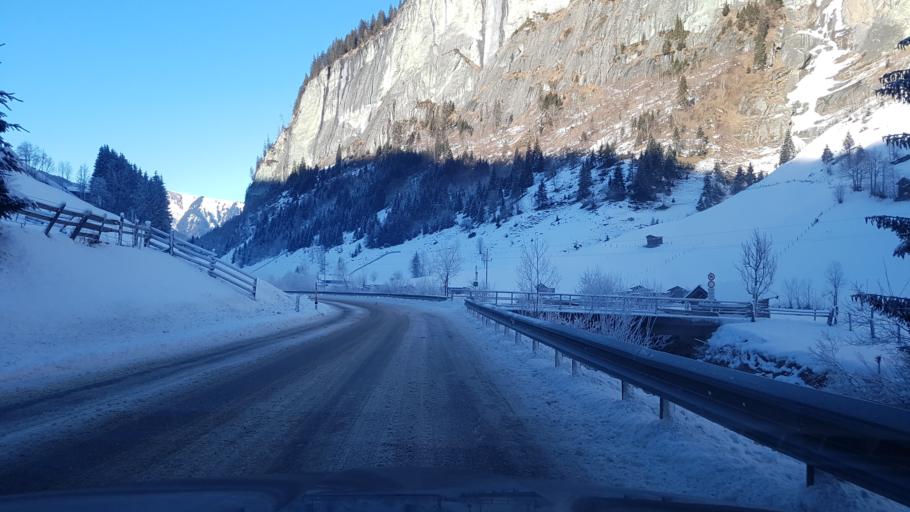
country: AT
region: Salzburg
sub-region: Politischer Bezirk Sankt Johann im Pongau
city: Huttschlag
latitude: 47.1711
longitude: 13.2432
